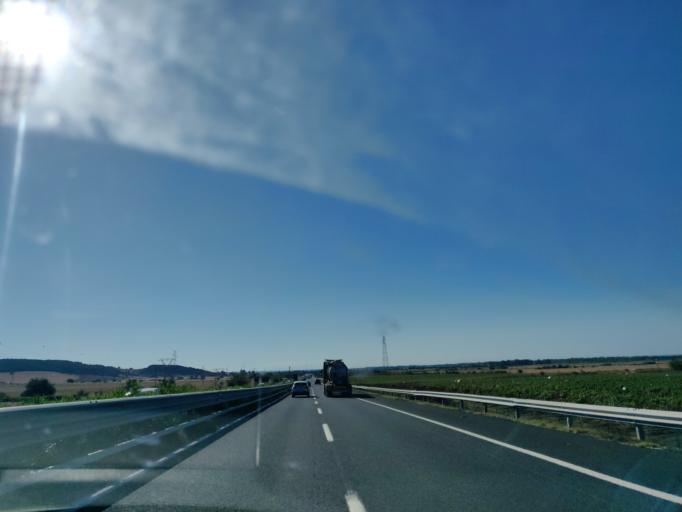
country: IT
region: Latium
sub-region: Citta metropolitana di Roma Capitale
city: Marina di Cerveteri
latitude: 42.0273
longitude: 11.9802
